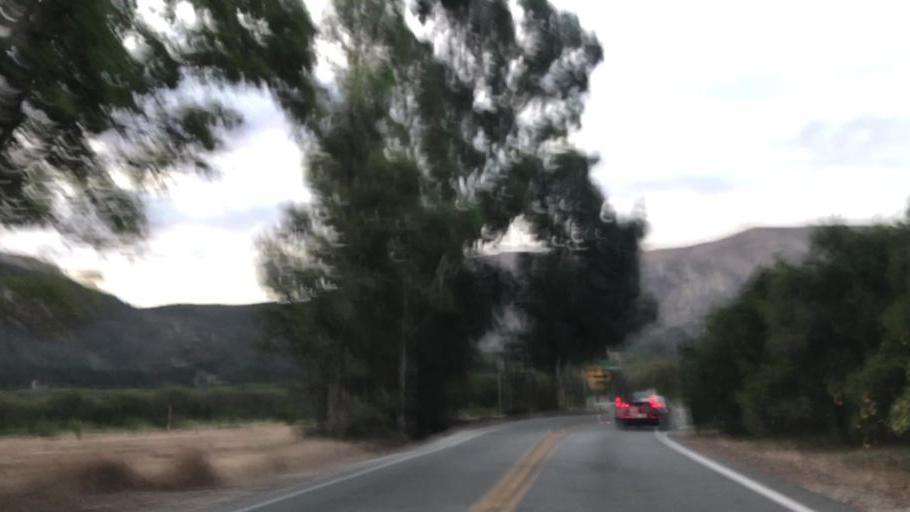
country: US
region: California
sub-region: Ventura County
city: Fillmore
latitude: 34.3652
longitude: -118.9421
